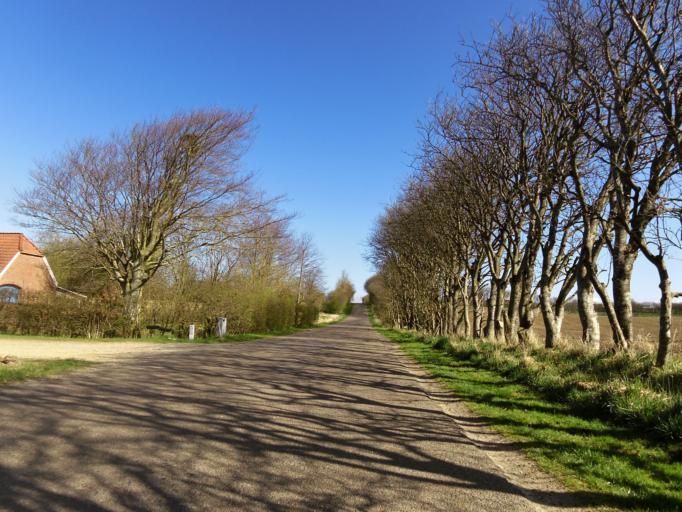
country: DK
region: Central Jutland
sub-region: Holstebro Kommune
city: Vinderup
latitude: 56.4337
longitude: 8.7592
